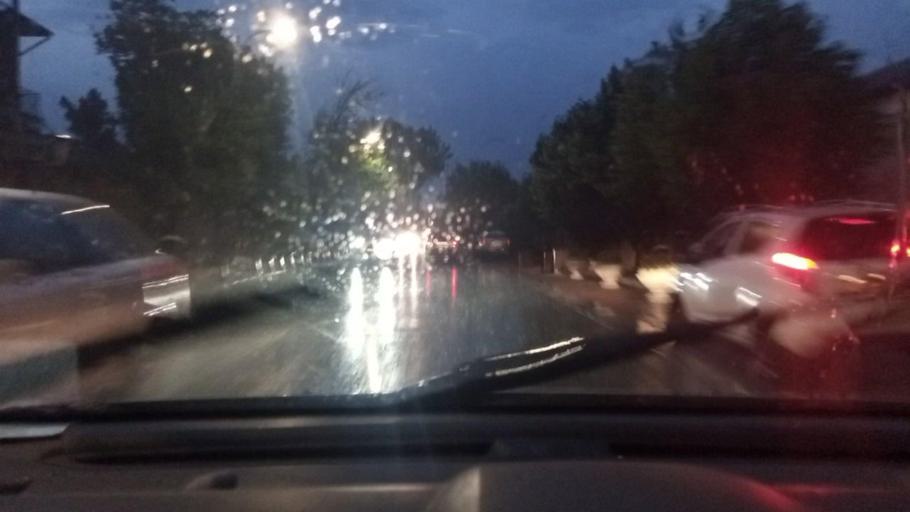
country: UZ
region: Toshkent
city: Salor
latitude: 41.3322
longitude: 69.3576
